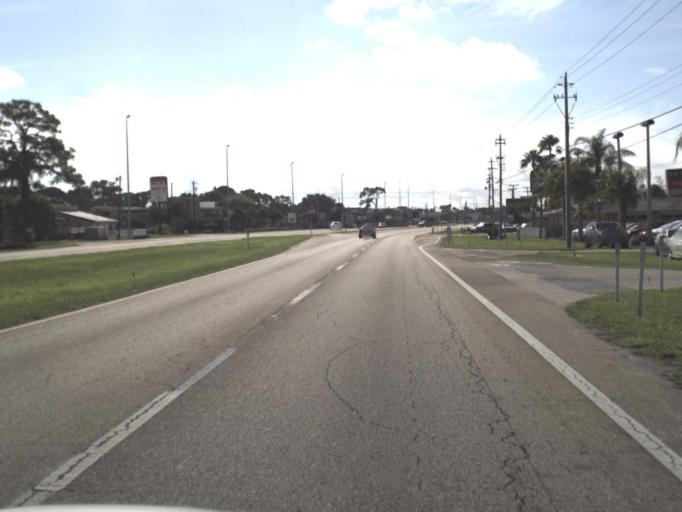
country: US
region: Florida
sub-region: Sarasota County
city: Gulf Gate Estates
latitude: 27.2530
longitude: -82.5159
